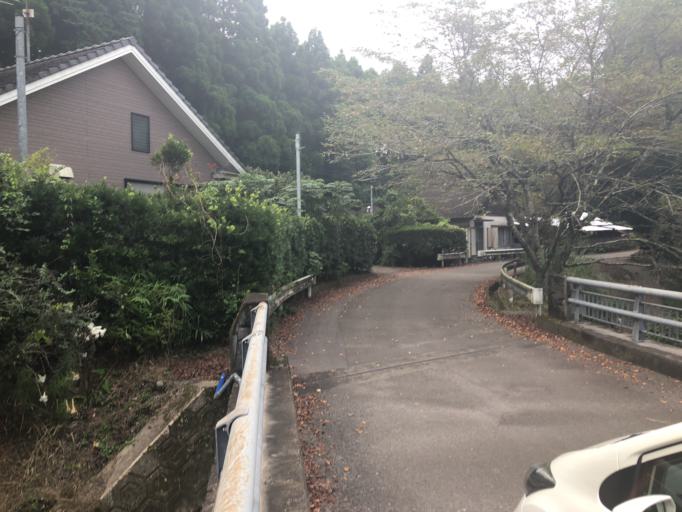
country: JP
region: Miyazaki
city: Kobayashi
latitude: 31.9936
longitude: 130.9200
